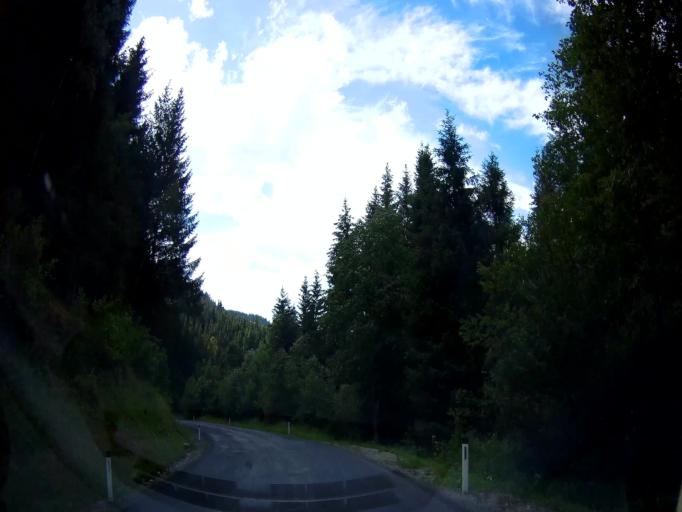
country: AT
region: Styria
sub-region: Politischer Bezirk Murau
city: Stadl an der Mur
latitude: 47.0483
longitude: 14.0003
